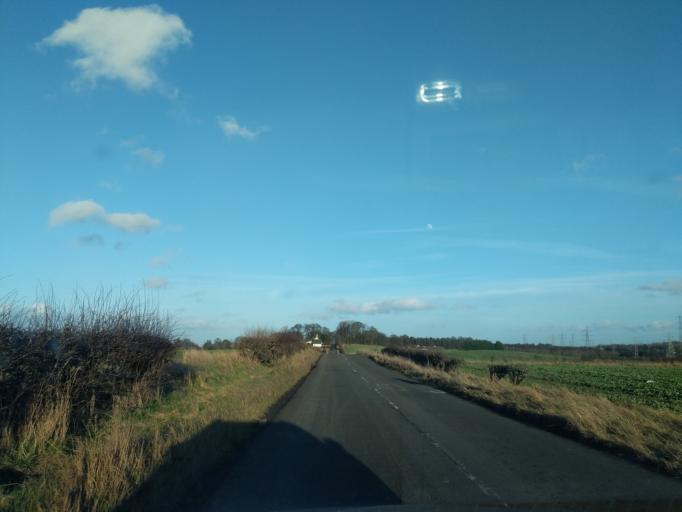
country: GB
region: Scotland
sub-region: Edinburgh
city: Balerno
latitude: 55.9016
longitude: -3.3361
